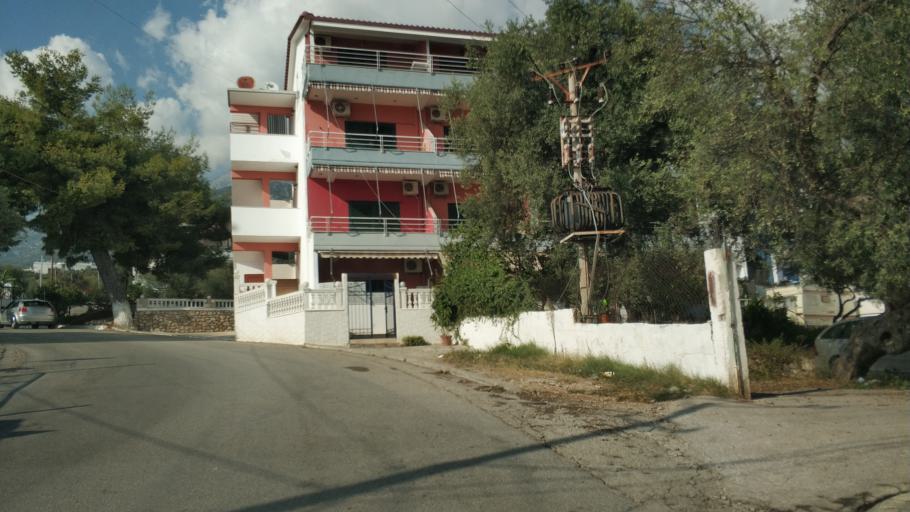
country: AL
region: Vlore
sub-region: Rrethi i Vlores
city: Vranisht
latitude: 40.1462
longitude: 19.6346
